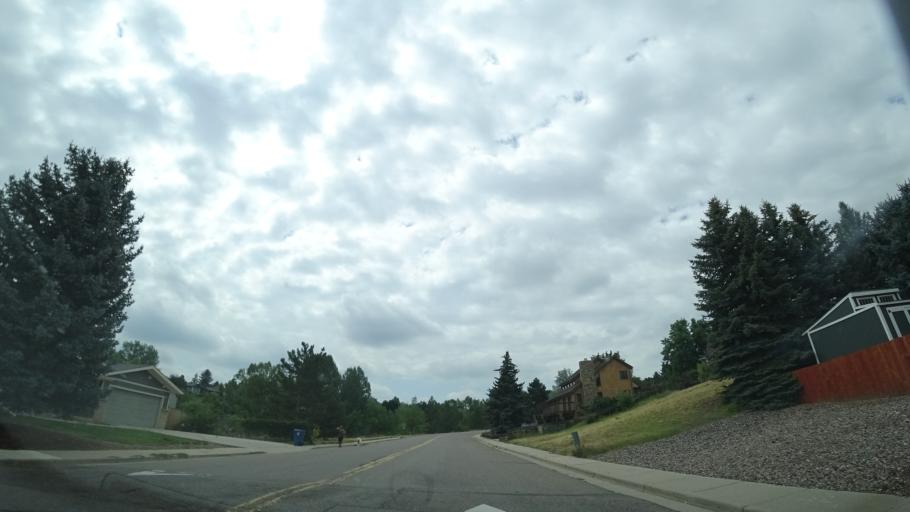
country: US
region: Colorado
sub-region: Jefferson County
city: West Pleasant View
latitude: 39.7155
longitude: -105.1594
